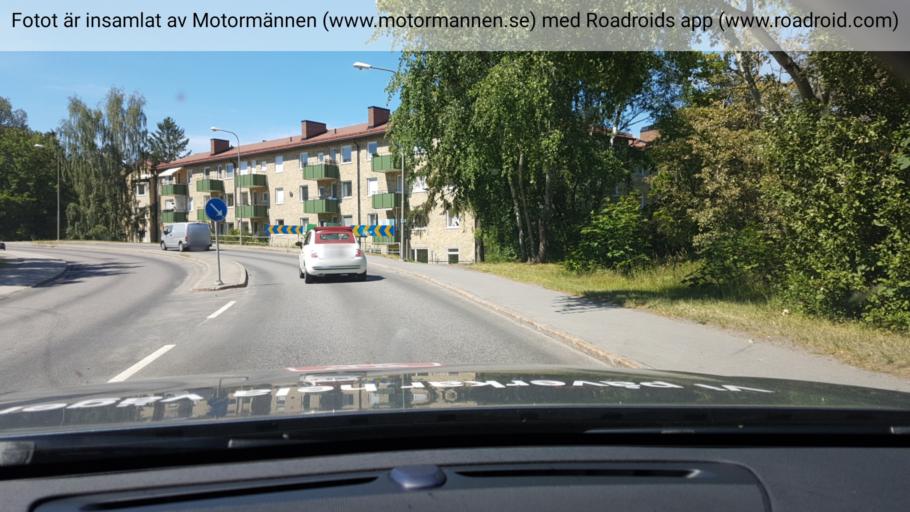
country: SE
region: Stockholm
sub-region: Stockholms Kommun
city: Arsta
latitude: 59.2709
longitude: 18.0471
